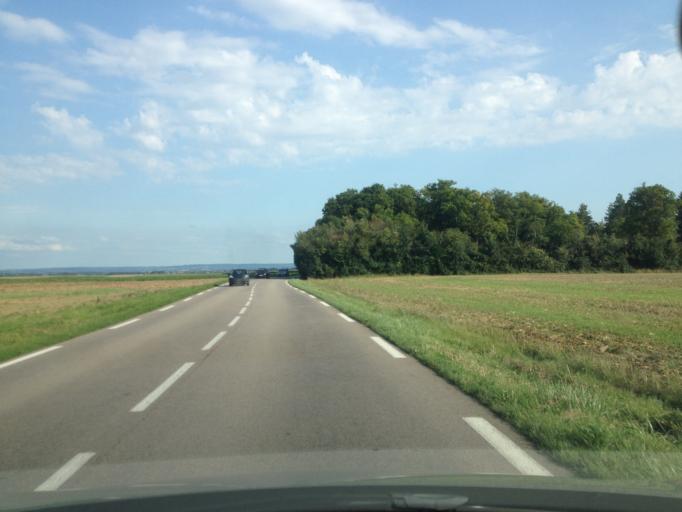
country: FR
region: Lower Normandy
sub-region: Departement du Calvados
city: Moult
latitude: 49.0794
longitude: -0.1437
